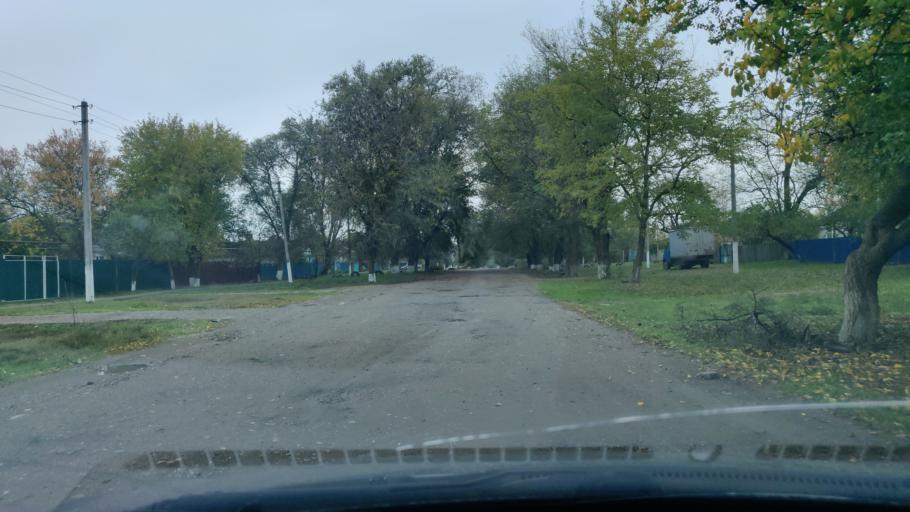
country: RU
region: Stavropol'skiy
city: Irgakly
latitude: 44.2428
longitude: 44.7211
